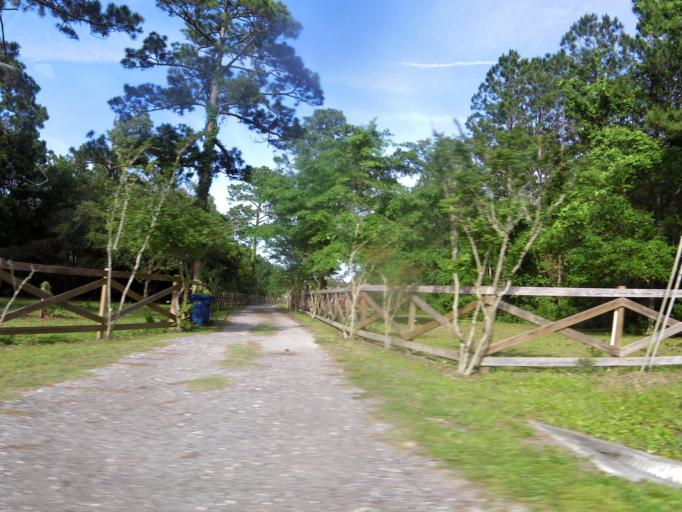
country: US
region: Florida
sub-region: Nassau County
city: Fernandina Beach
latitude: 30.5260
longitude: -81.4828
